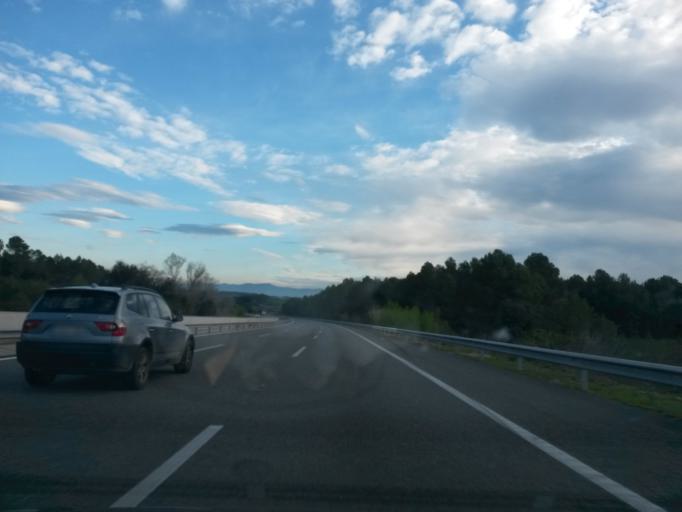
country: ES
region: Catalonia
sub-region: Provincia de Girona
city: Bascara
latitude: 42.1409
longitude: 2.9186
